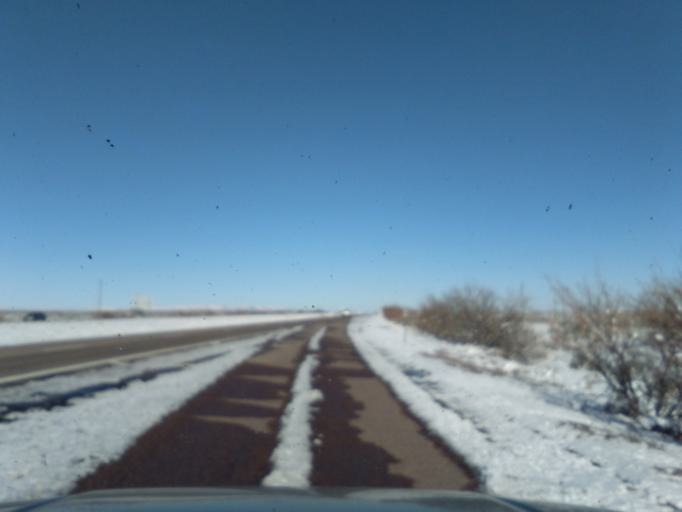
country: US
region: New Mexico
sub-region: Socorro County
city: Socorro
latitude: 33.6382
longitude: -107.1189
